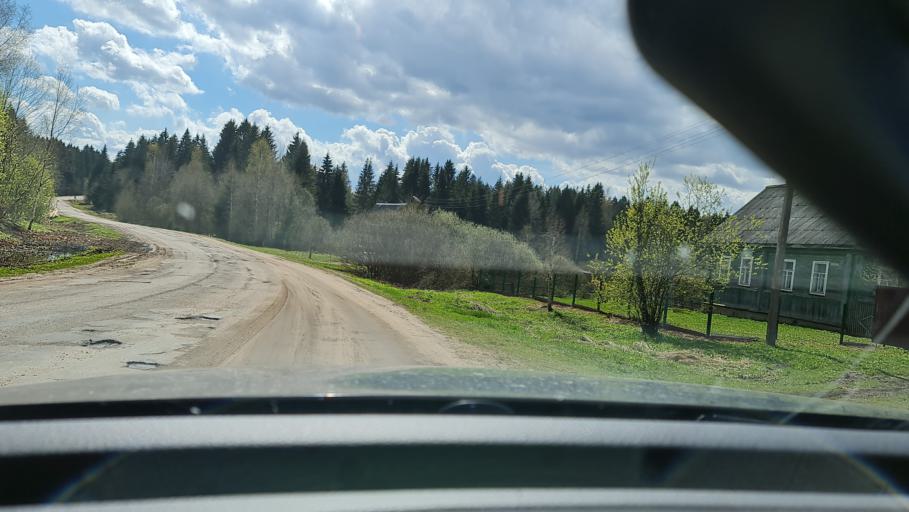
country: RU
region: Tverskaya
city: Toropets
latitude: 56.6416
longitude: 31.4218
